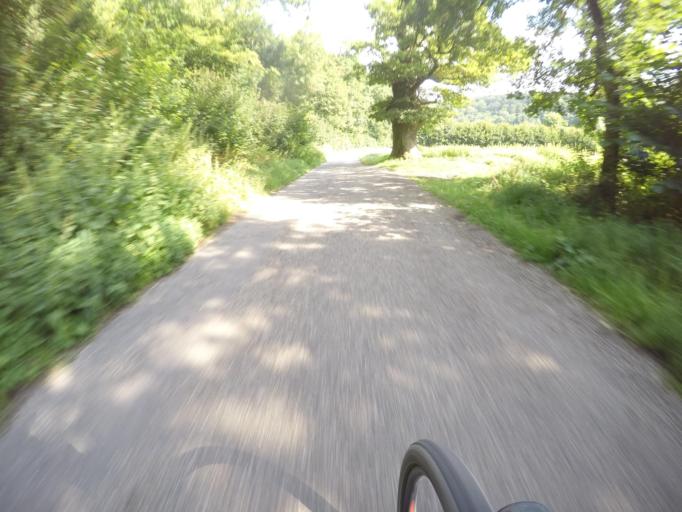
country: DE
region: Baden-Wuerttemberg
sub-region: Karlsruhe Region
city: Niefern-Oschelbronn
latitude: 48.9397
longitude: 8.7755
